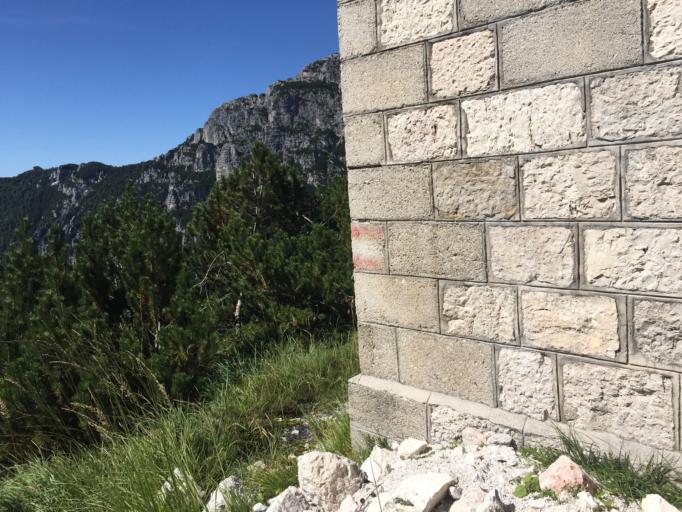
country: IT
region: Friuli Venezia Giulia
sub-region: Provincia di Udine
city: Dogna
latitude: 46.4389
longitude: 13.2677
